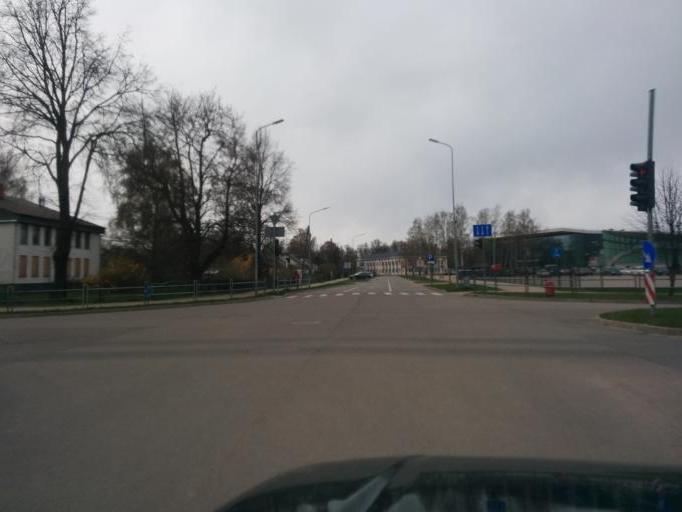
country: LV
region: Jelgava
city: Jelgava
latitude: 56.6589
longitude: 23.7545
